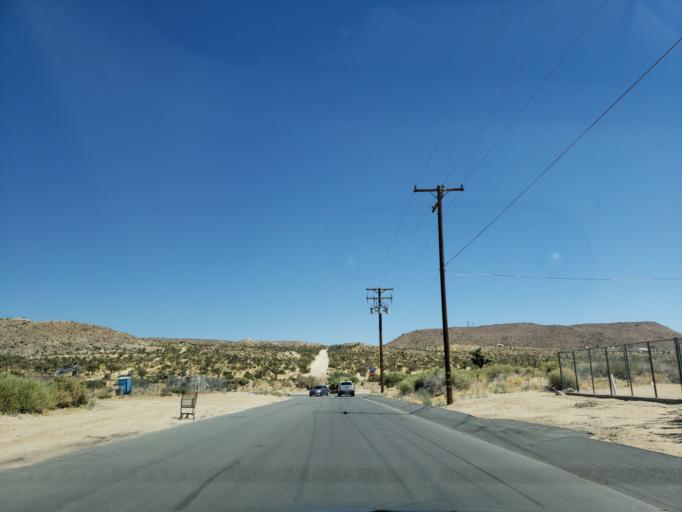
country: US
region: California
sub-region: San Bernardino County
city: Yucca Valley
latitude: 34.1343
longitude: -116.3959
